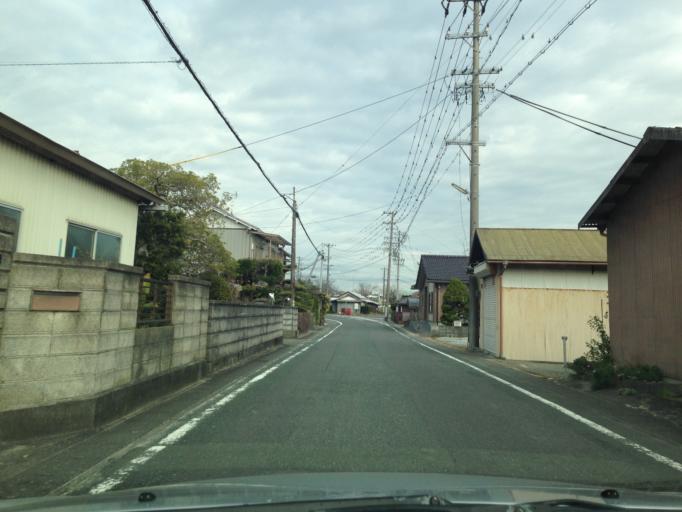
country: JP
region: Shizuoka
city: Fukuroi
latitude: 34.7616
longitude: 137.9598
